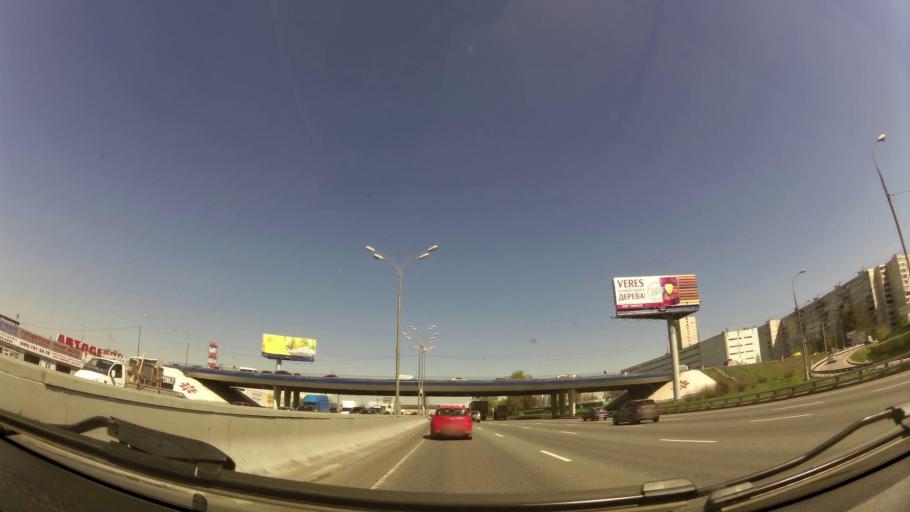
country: RU
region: Moscow
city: Strogino
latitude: 55.8083
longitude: 37.3883
